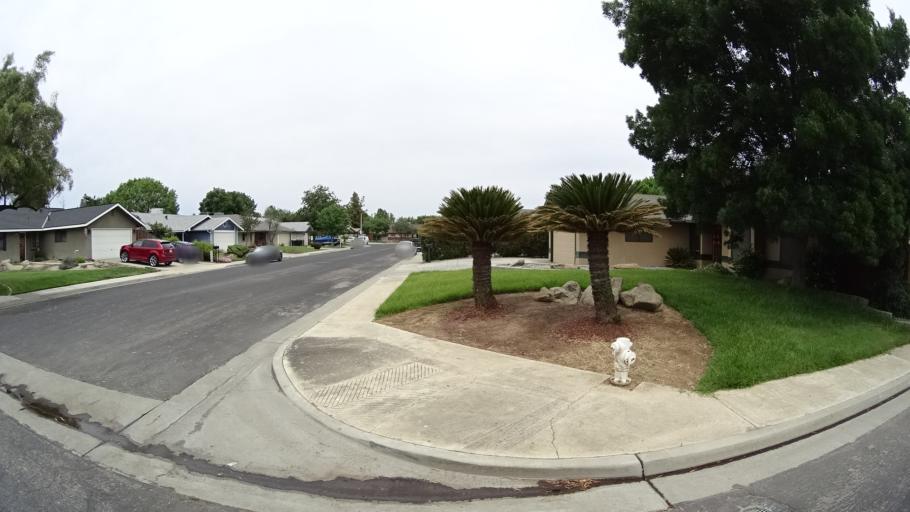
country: US
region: California
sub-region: Kings County
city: Hanford
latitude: 36.3536
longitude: -119.6357
